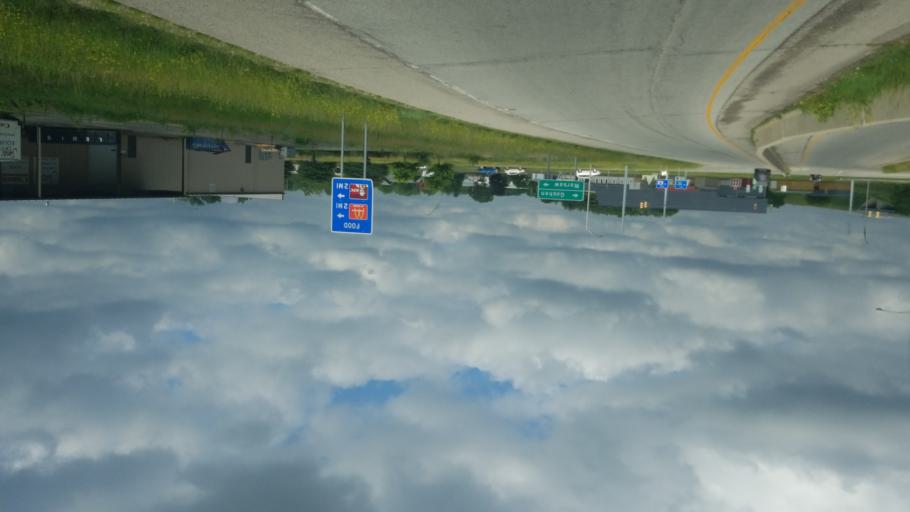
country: US
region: Indiana
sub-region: Kosciusko County
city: Warsaw
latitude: 41.2654
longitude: -85.8542
